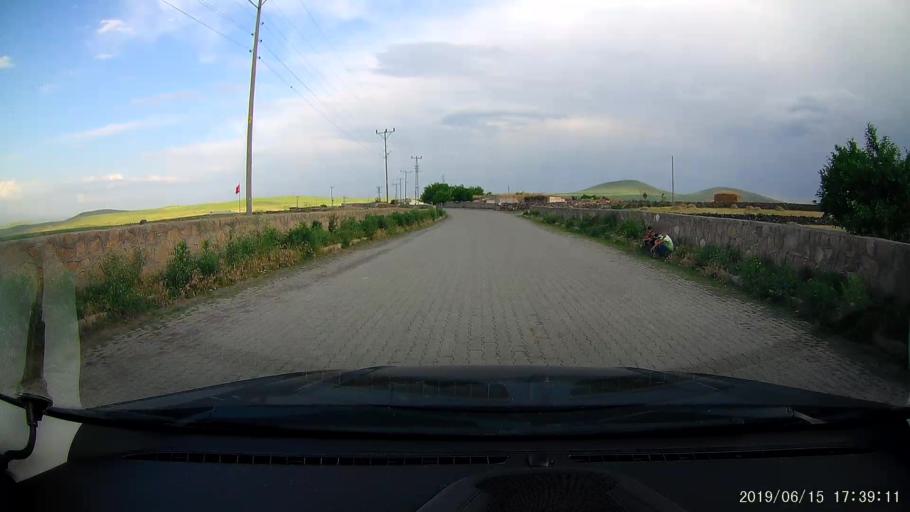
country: TR
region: Kars
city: Basgedikler
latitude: 40.5174
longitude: 43.5693
